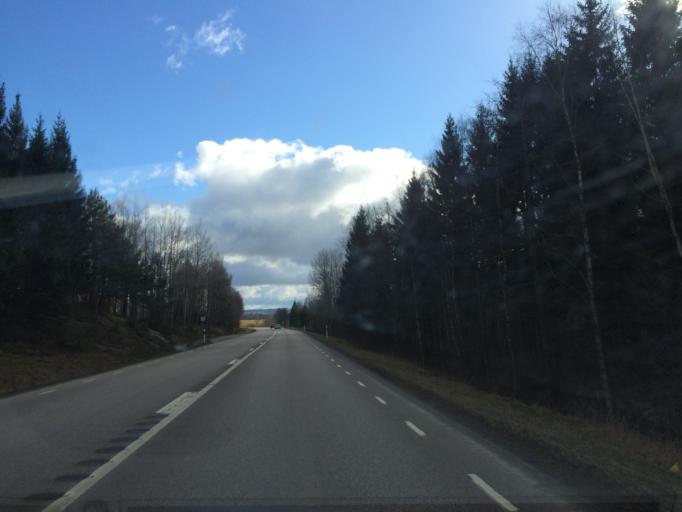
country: SE
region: Vaestra Goetaland
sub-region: Skara Kommun
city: Skara
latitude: 58.2997
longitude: 13.4696
